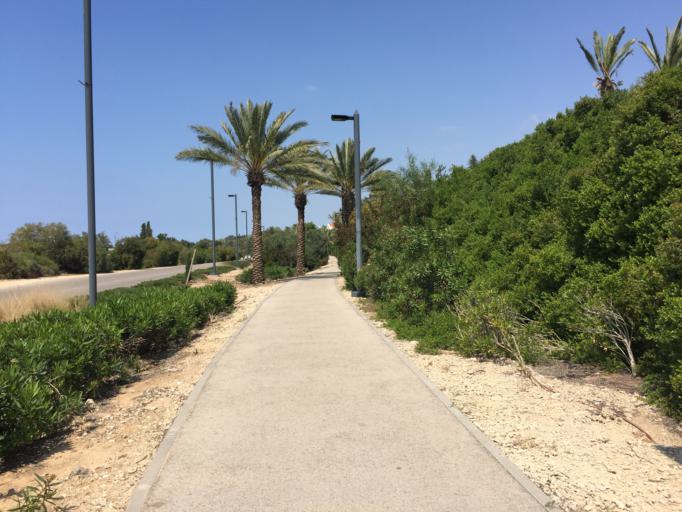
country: IL
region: Haifa
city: Qesarya
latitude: 32.4915
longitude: 34.9038
